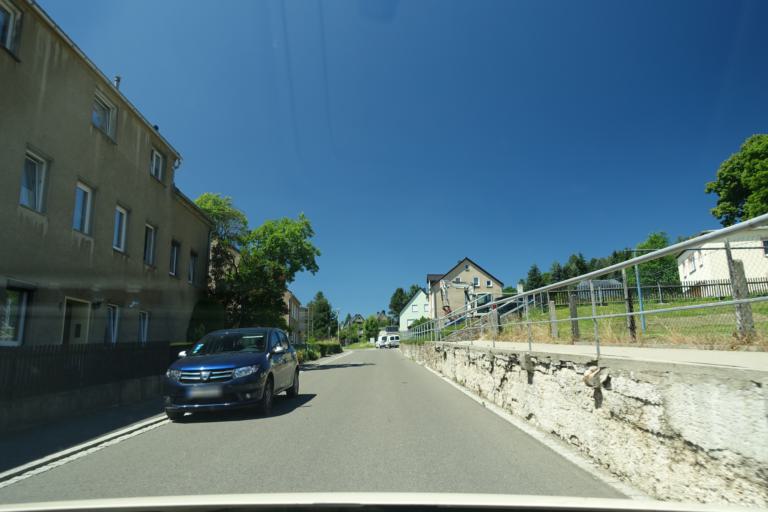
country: DE
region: Saxony
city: Eppendorf
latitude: 50.7995
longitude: 13.2270
